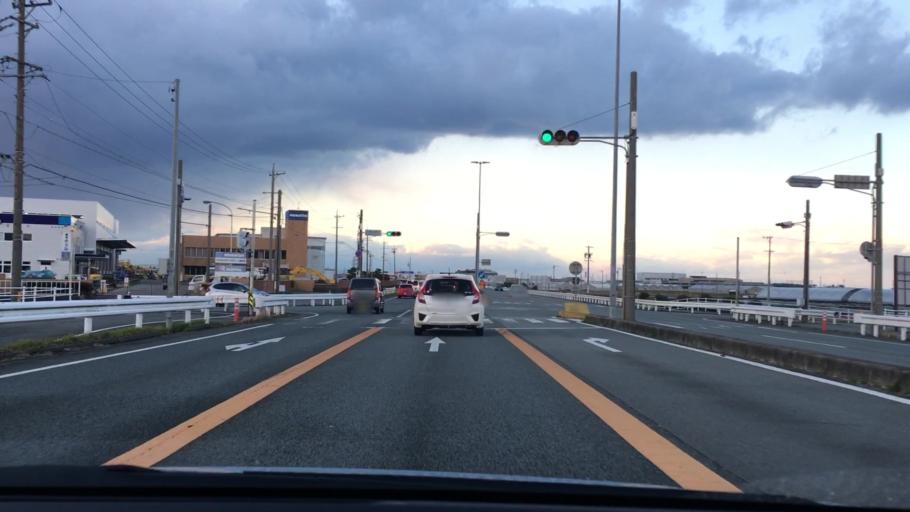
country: JP
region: Mie
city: Ise
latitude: 34.5250
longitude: 136.6841
